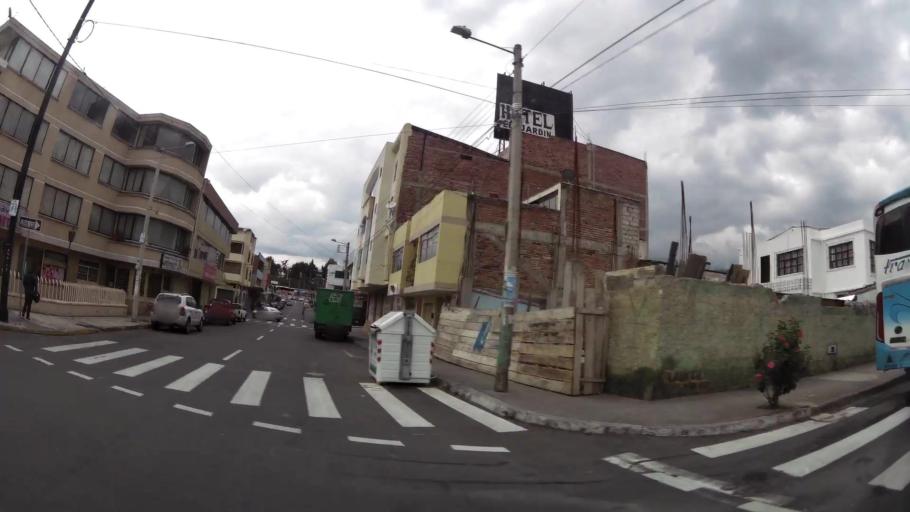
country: EC
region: Tungurahua
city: Ambato
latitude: -1.2341
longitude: -78.6154
